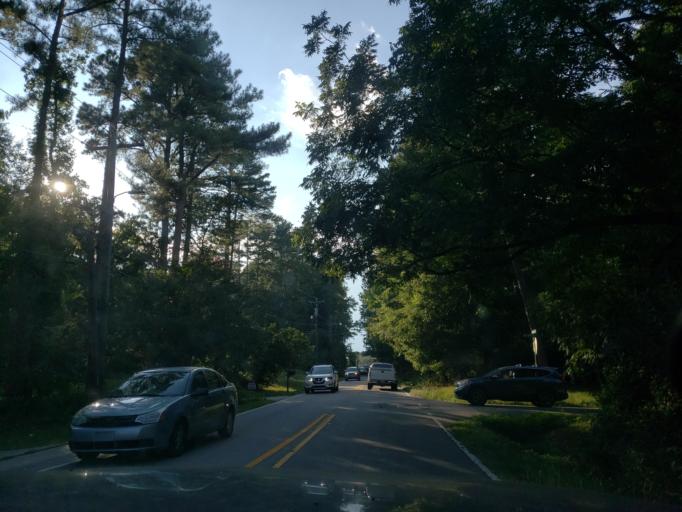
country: US
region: North Carolina
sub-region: Durham County
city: Durham
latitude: 35.9714
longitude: -78.9295
